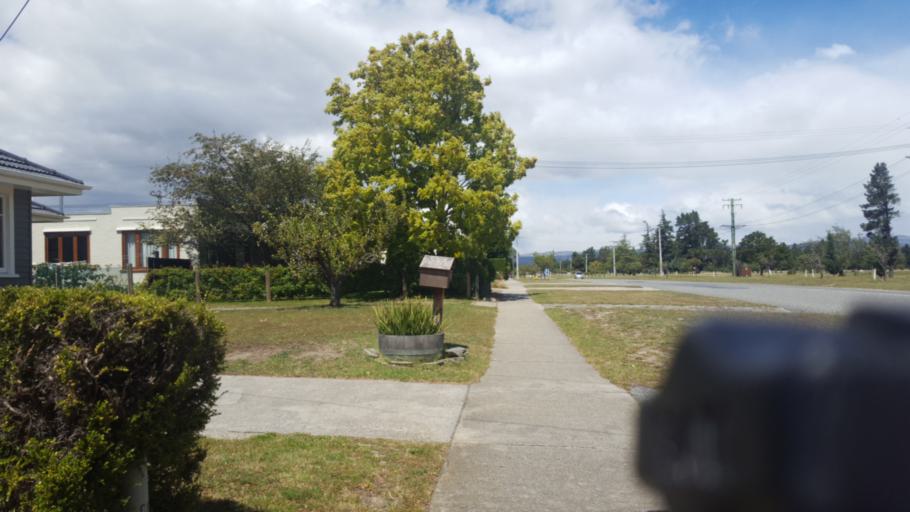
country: NZ
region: Otago
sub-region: Queenstown-Lakes District
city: Wanaka
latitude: -45.1924
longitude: 169.3240
